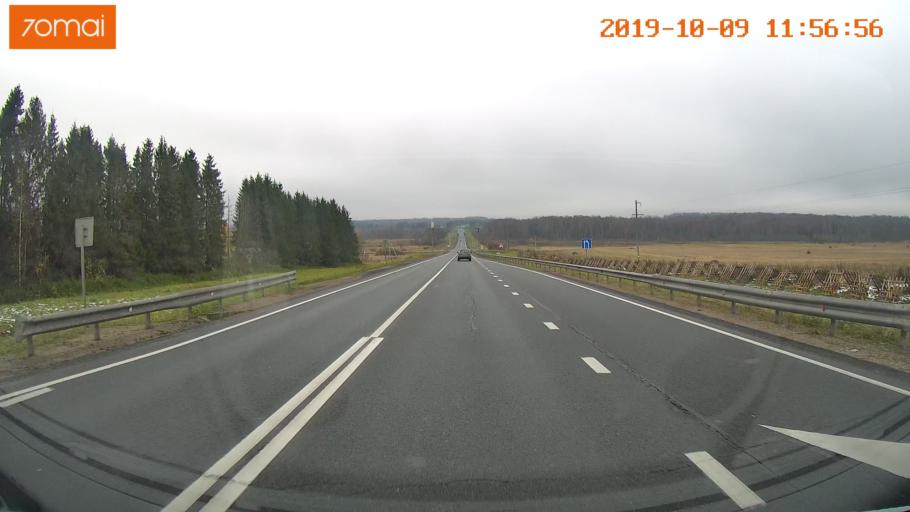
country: RU
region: Vologda
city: Gryazovets
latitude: 58.7385
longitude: 40.2900
